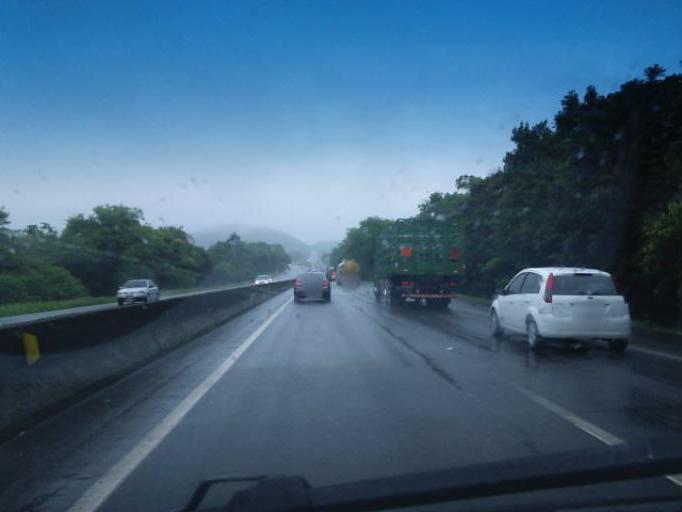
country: BR
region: Santa Catarina
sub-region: Joinville
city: Joinville
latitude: -26.1111
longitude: -48.8745
